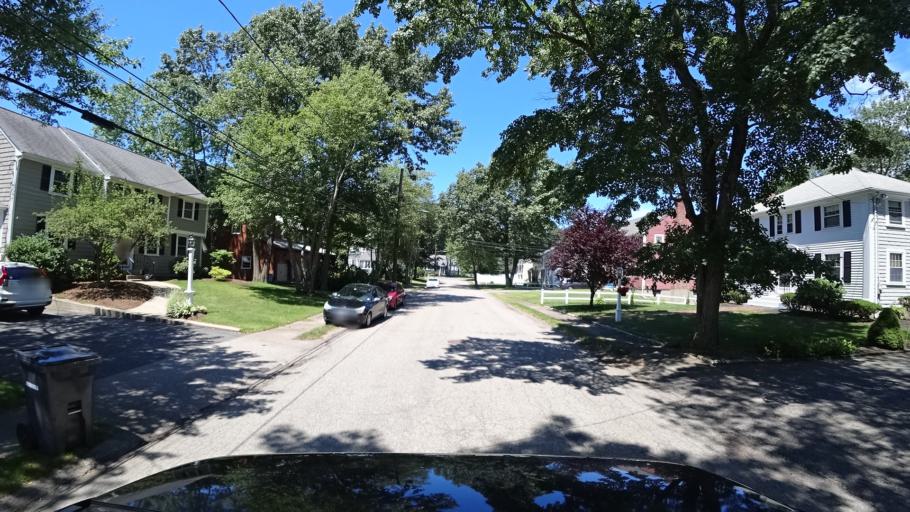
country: US
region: Massachusetts
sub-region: Norfolk County
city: Dedham
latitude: 42.2194
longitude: -71.1570
